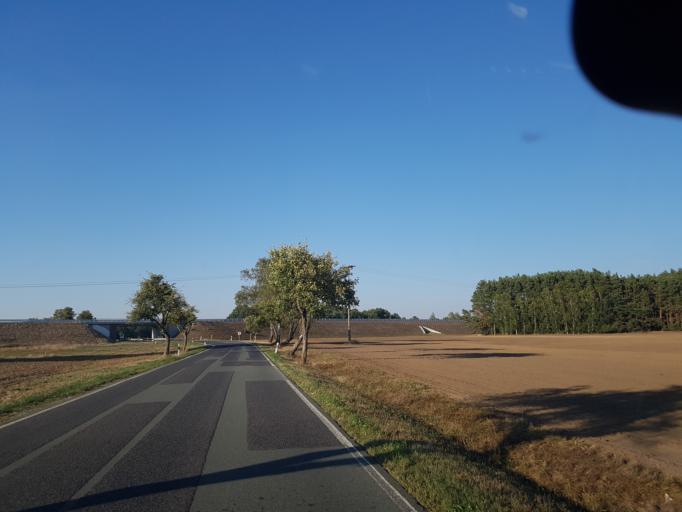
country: DE
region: Brandenburg
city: Bad Liebenwerda
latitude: 51.5025
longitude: 13.4052
